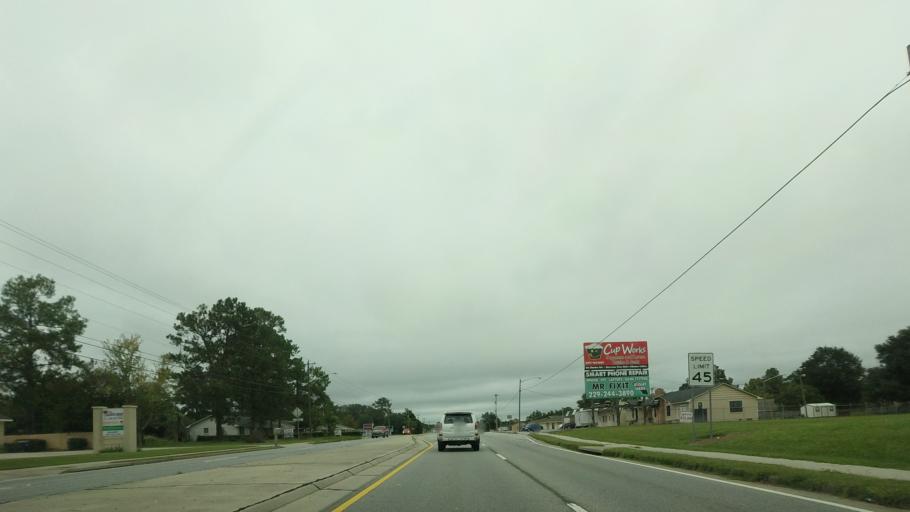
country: US
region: Georgia
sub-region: Lowndes County
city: Valdosta
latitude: 30.8855
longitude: -83.2724
